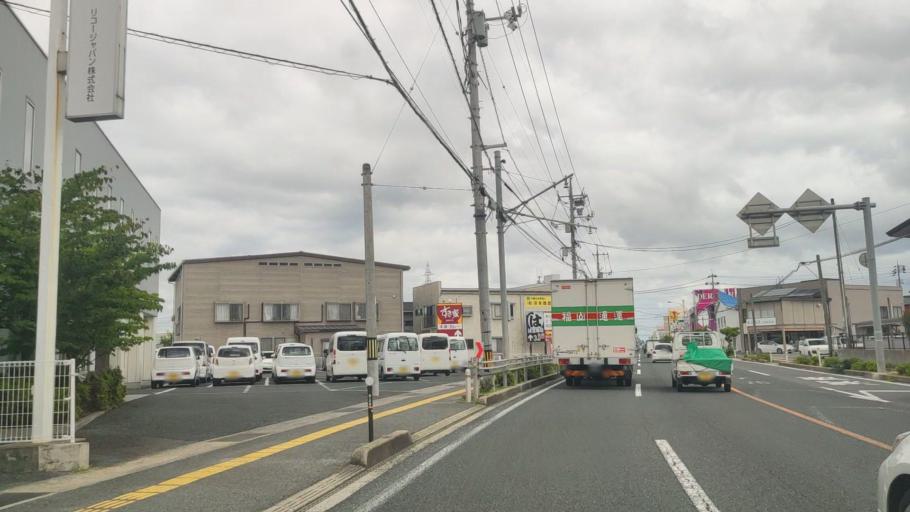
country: JP
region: Tottori
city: Yonago
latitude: 35.4328
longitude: 133.3523
